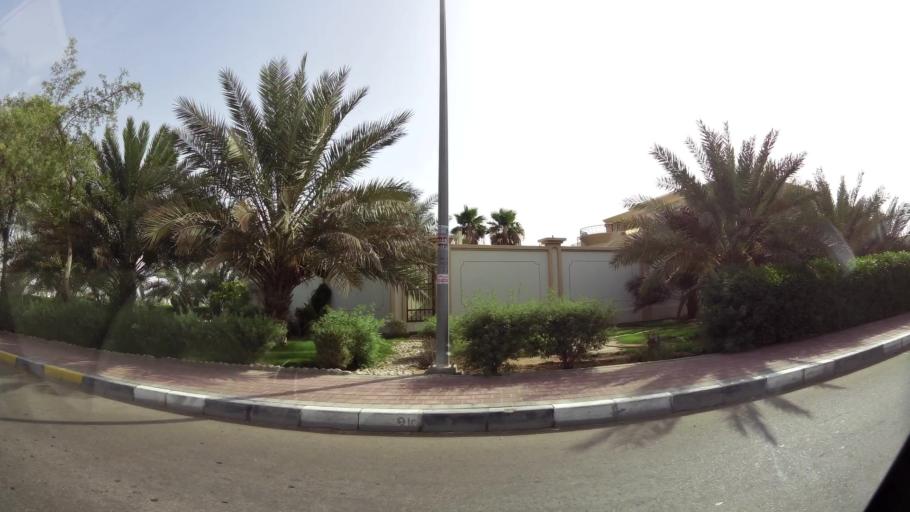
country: AE
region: Abu Dhabi
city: Al Ain
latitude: 24.1430
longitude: 55.7031
